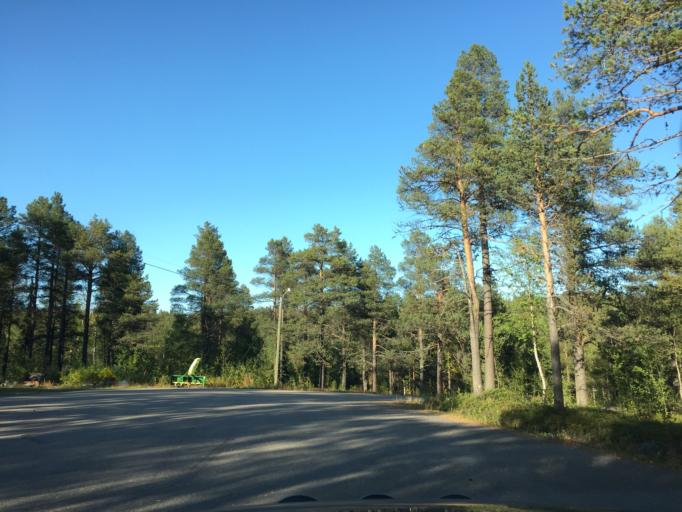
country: SE
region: Norrbotten
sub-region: Gallivare Kommun
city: Malmberget
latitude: 67.6548
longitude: 21.0316
